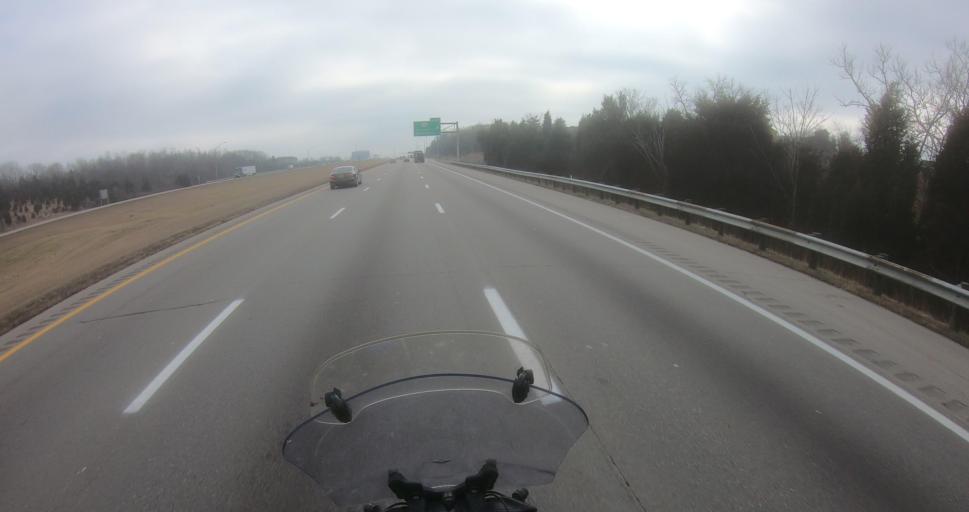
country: US
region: Ohio
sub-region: Montgomery County
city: West Carrollton City
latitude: 39.6510
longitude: -84.2344
